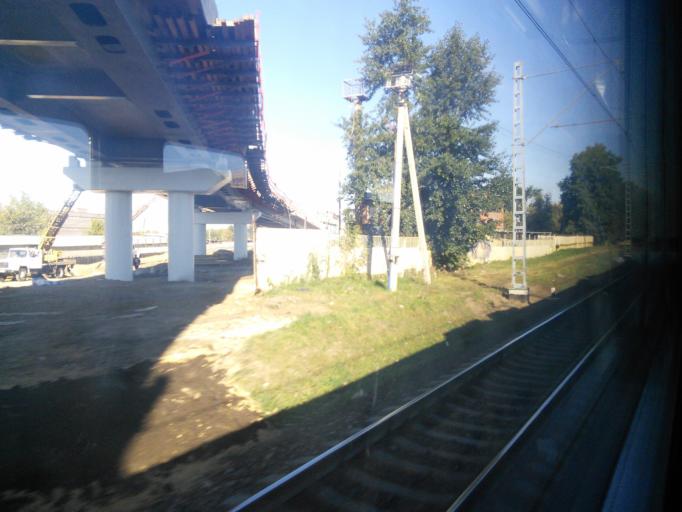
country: RU
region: Moscow
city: Tekstil'shchiki
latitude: 55.7164
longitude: 37.7239
